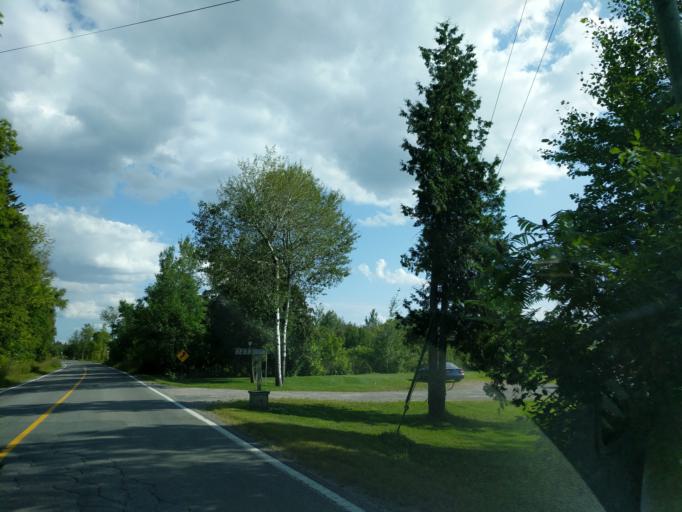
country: CA
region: Quebec
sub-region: Outaouais
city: Gatineau
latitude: 45.4707
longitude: -75.8517
